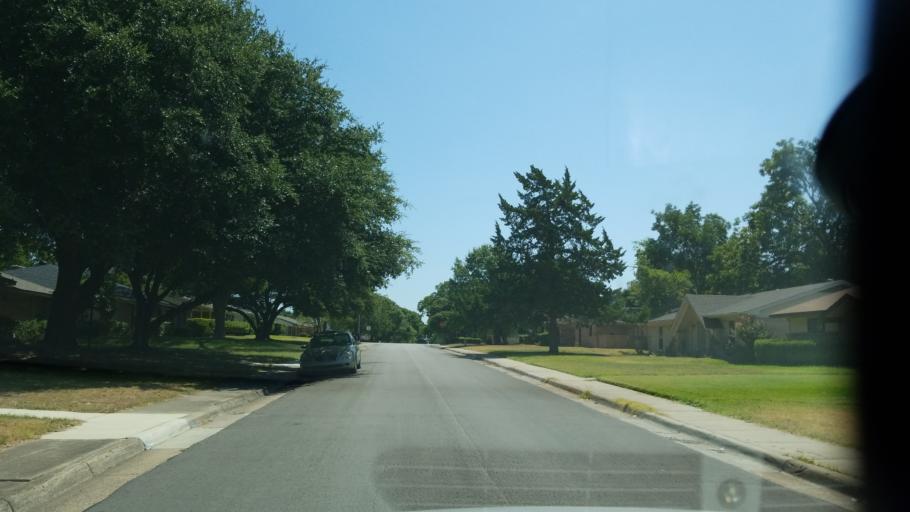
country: US
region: Texas
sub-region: Dallas County
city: Duncanville
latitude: 32.6533
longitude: -96.8965
